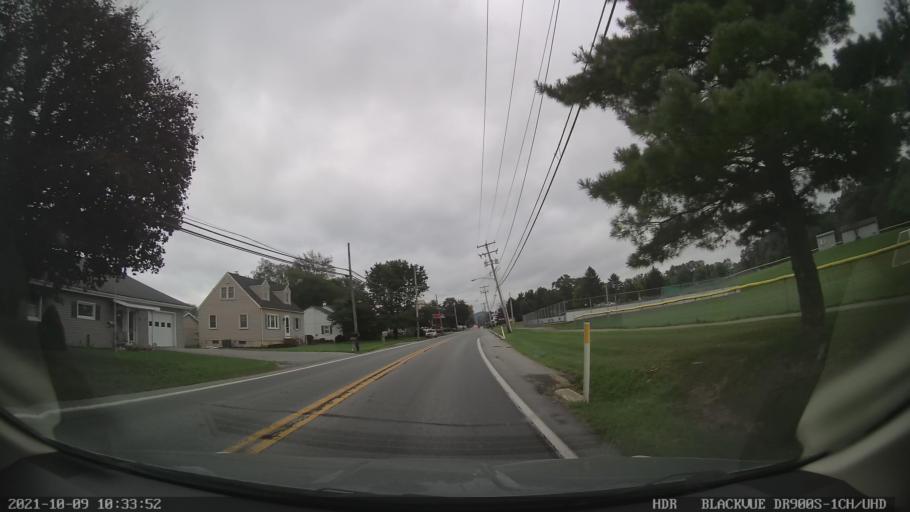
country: US
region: Pennsylvania
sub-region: Berks County
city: Topton
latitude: 40.5049
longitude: -75.6638
